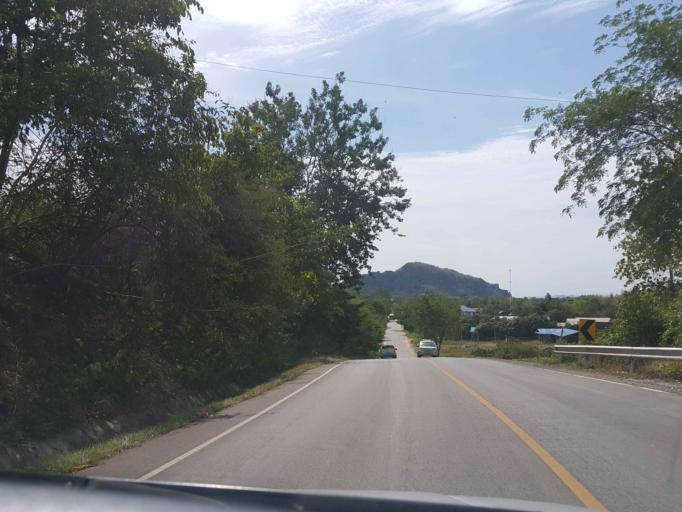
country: TH
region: Sukhothai
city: Thung Saliam
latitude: 17.3358
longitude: 99.4769
